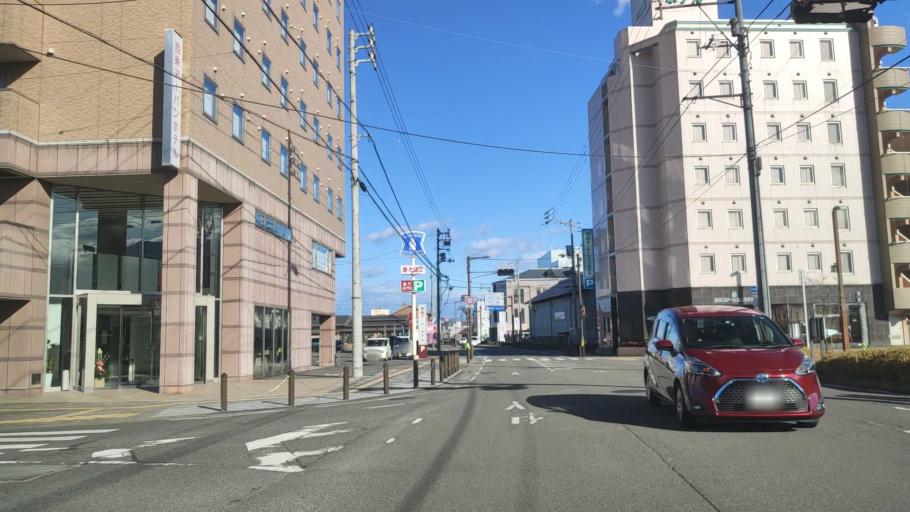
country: JP
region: Ehime
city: Saijo
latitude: 33.9130
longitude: 133.1871
